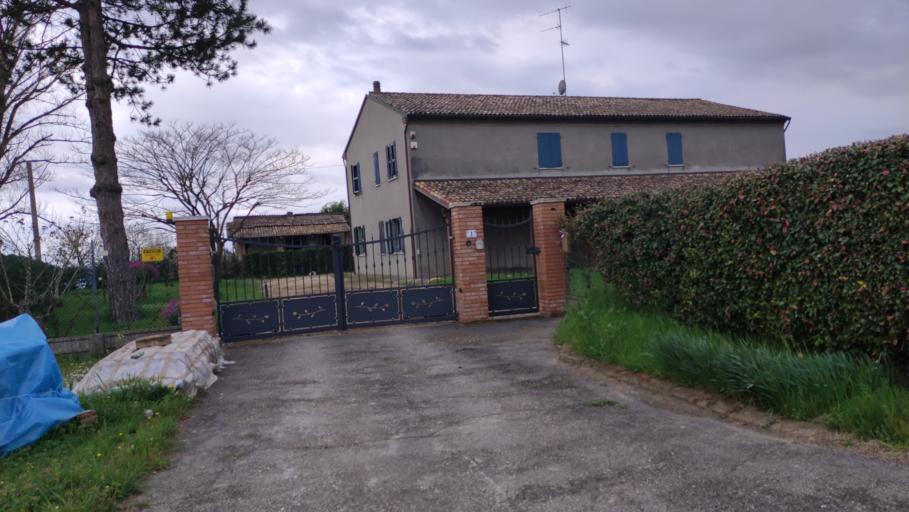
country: IT
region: Emilia-Romagna
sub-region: Provincia di Ravenna
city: Russi
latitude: 44.3961
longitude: 12.0487
